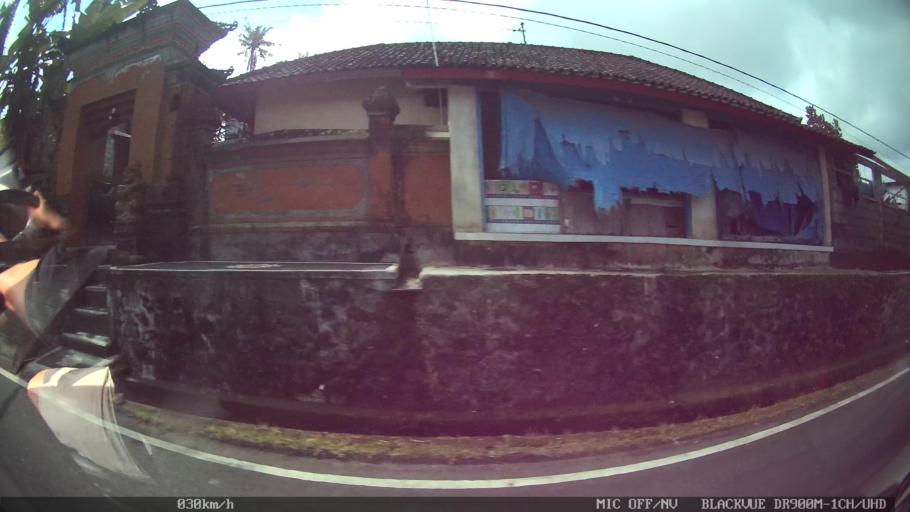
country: ID
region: Bali
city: Banjar Pesalakan
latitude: -8.5201
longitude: 115.3044
